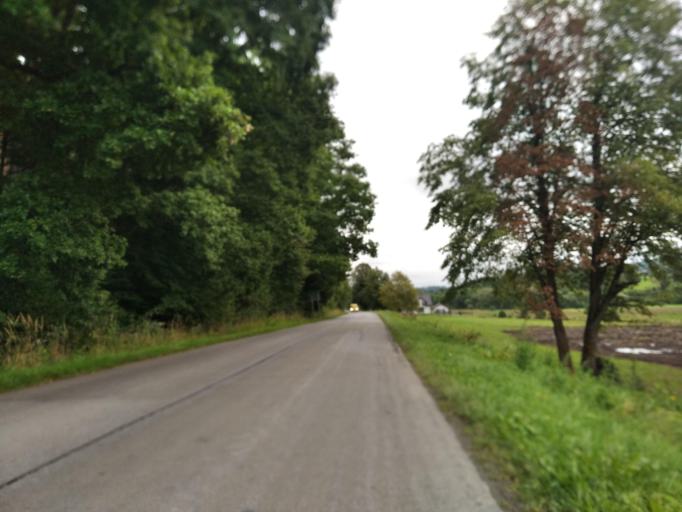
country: PL
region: Subcarpathian Voivodeship
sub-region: Powiat przemyski
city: Bircza
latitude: 49.6871
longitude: 22.3983
